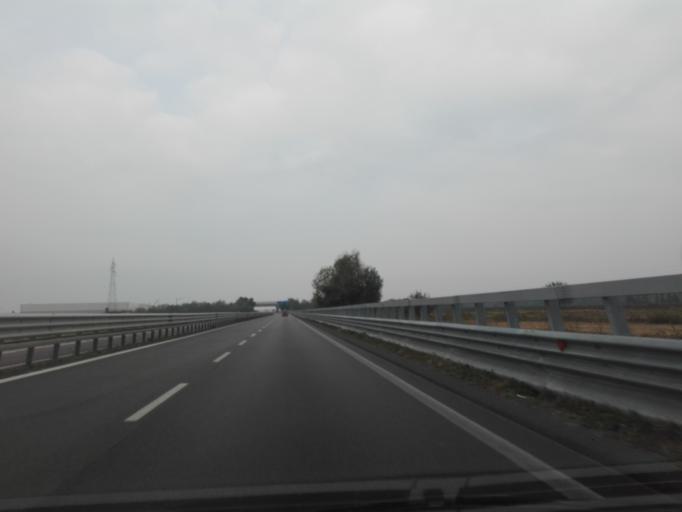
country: IT
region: Veneto
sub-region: Provincia di Verona
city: Ca' degli Oppi
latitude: 45.3069
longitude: 11.1286
